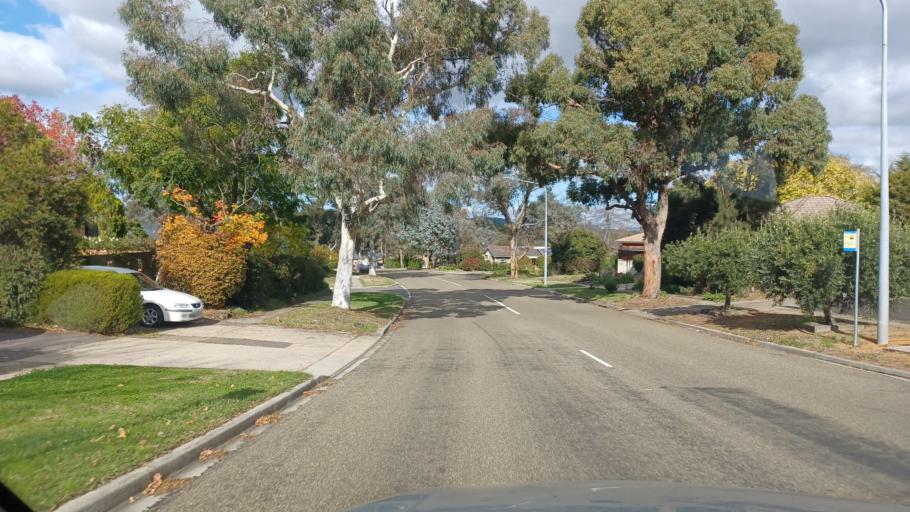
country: AU
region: Australian Capital Territory
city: Belconnen
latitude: -35.2042
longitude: 149.0602
